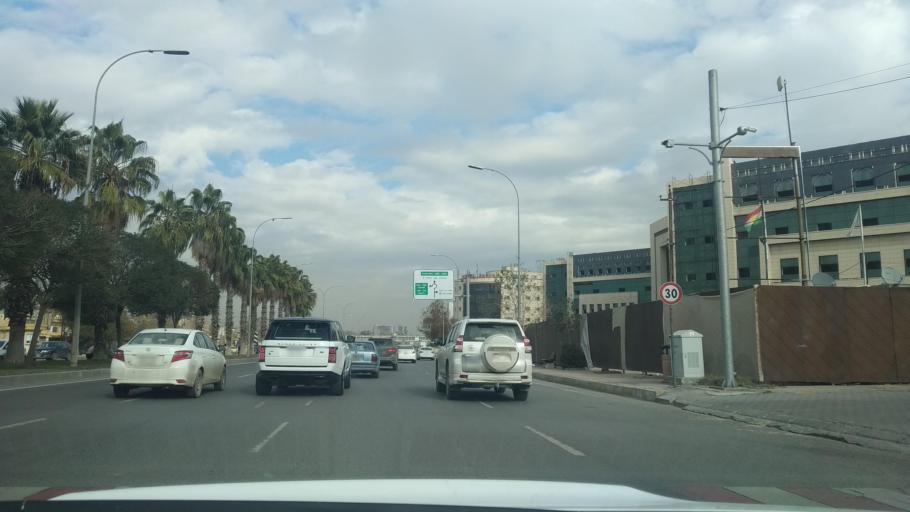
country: IQ
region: Arbil
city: Erbil
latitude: 36.1872
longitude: 43.9938
